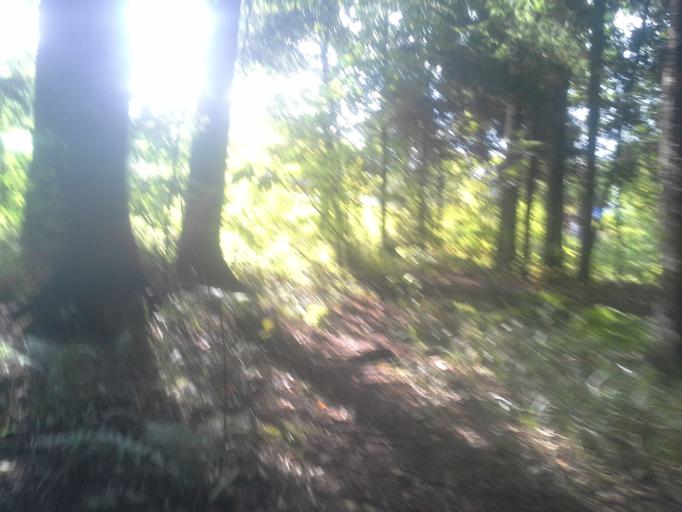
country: RU
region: Moskovskaya
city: Kievskij
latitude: 55.3450
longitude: 36.9617
